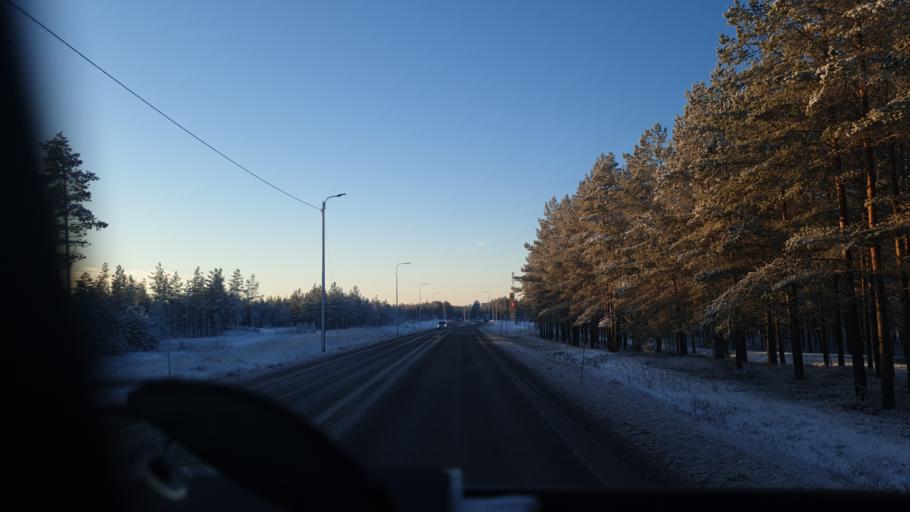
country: FI
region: Northern Ostrobothnia
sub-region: Ylivieska
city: Kalajoki
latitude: 64.2327
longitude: 23.8233
